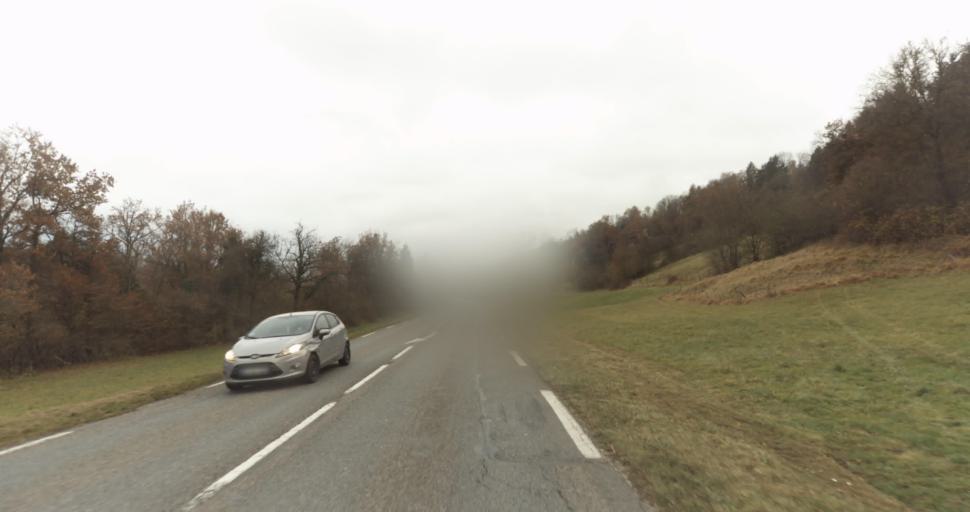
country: FR
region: Rhone-Alpes
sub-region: Departement de la Haute-Savoie
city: Groisy
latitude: 45.9924
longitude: 6.1723
